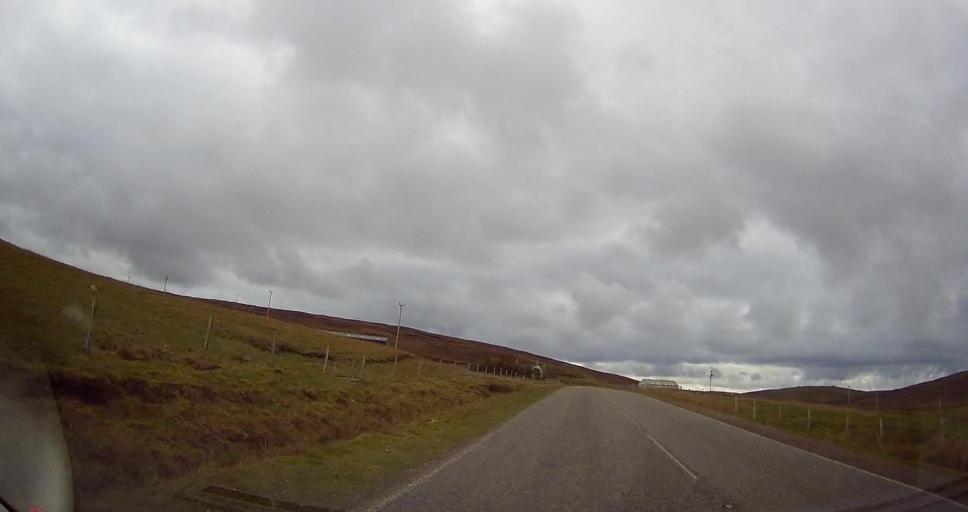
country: GB
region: Scotland
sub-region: Shetland Islands
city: Shetland
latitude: 60.6054
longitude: -1.1076
